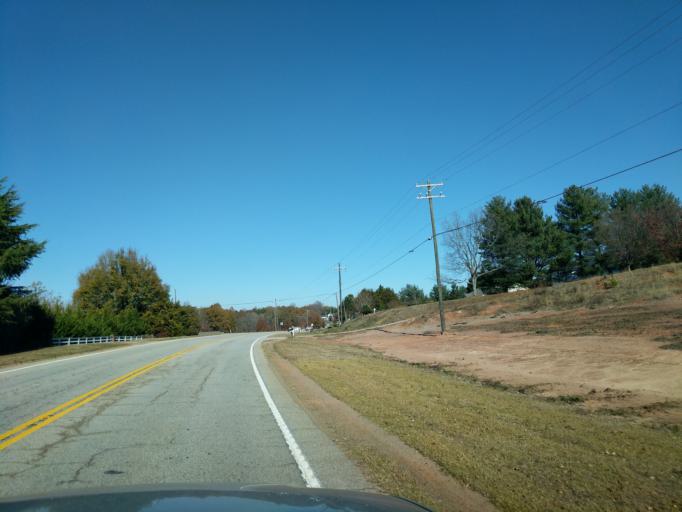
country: US
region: South Carolina
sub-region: Spartanburg County
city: Inman Mills
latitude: 35.0370
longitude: -82.1851
